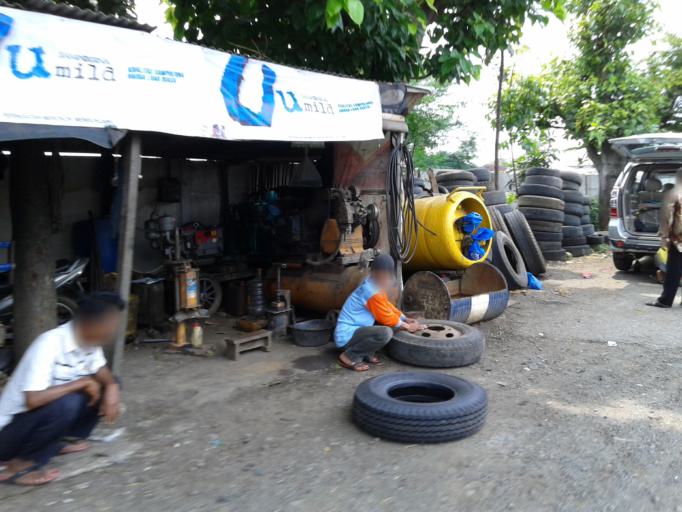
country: ID
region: East Java
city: Lawang
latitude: -7.8611
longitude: 112.6866
